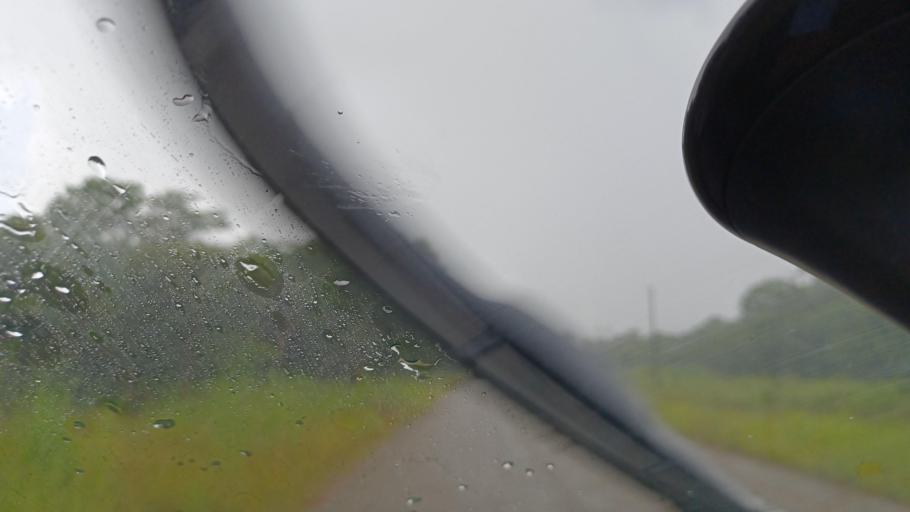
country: ZM
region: North-Western
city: Kasempa
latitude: -13.0909
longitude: 25.9406
